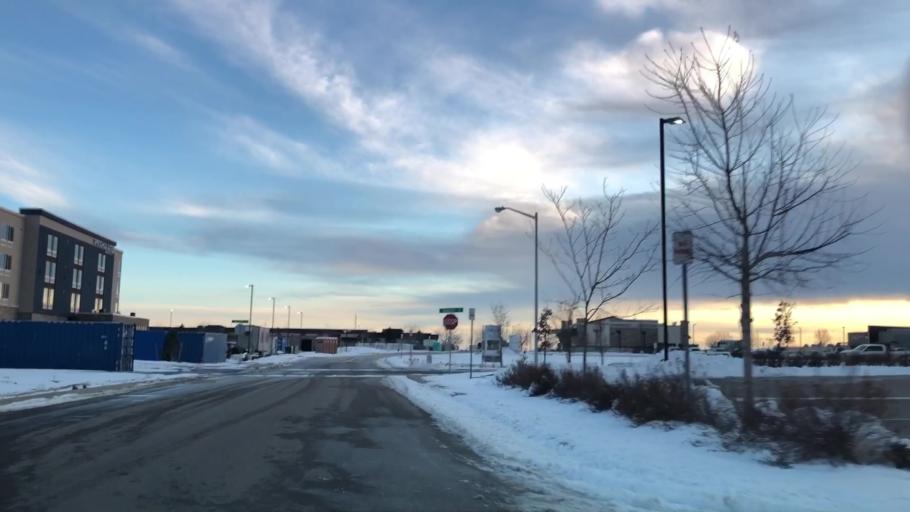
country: US
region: Colorado
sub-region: Weld County
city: Windsor
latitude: 40.4381
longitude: -104.9804
